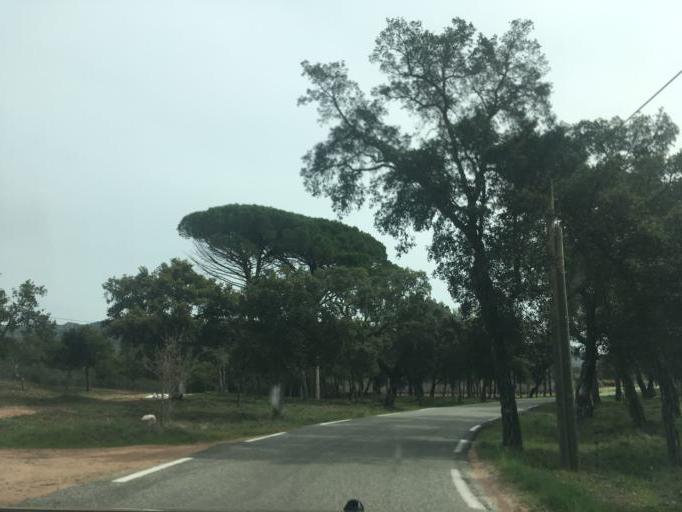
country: FR
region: Provence-Alpes-Cote d'Azur
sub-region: Departement du Var
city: Le Muy
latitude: 43.5094
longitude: 6.6080
